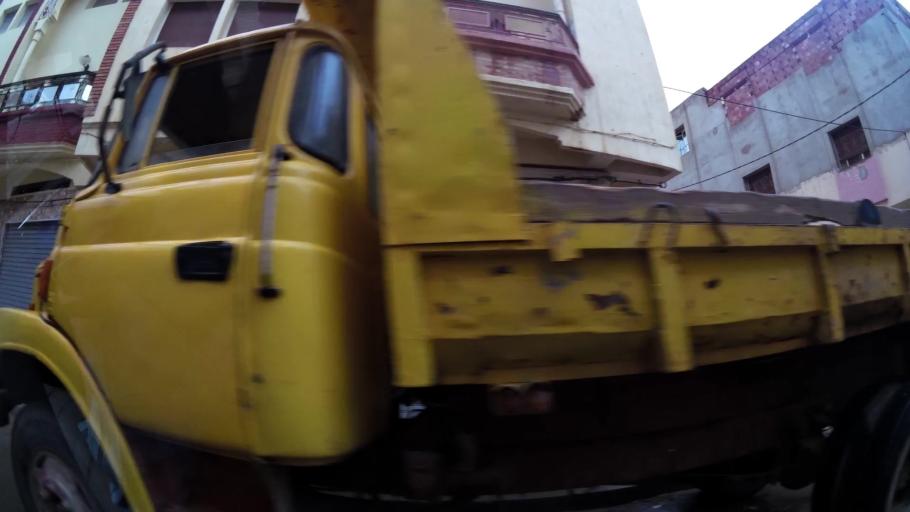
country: MA
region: Oriental
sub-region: Nador
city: Nador
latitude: 35.1704
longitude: -2.9415
